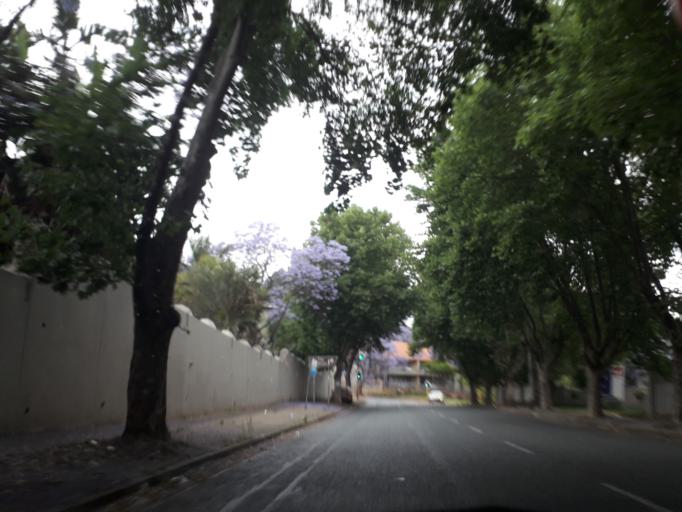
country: ZA
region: Gauteng
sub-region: City of Johannesburg Metropolitan Municipality
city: Johannesburg
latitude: -26.1704
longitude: 28.0553
